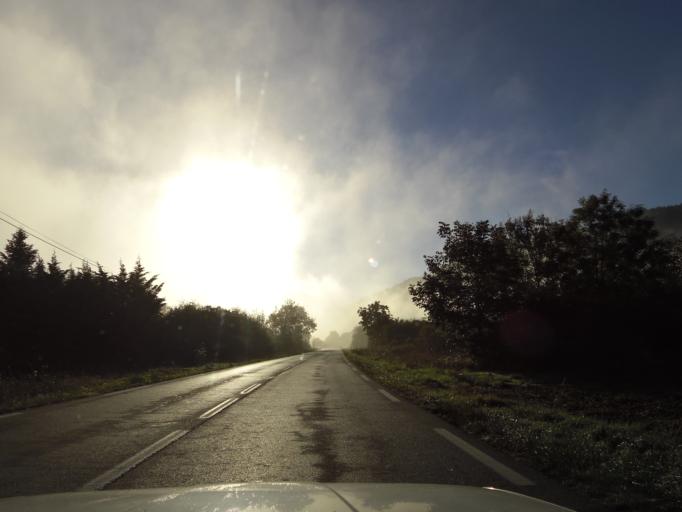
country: FR
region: Rhone-Alpes
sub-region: Departement de l'Ain
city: Saint-Sorlin-en-Bugey
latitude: 45.8770
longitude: 5.3535
